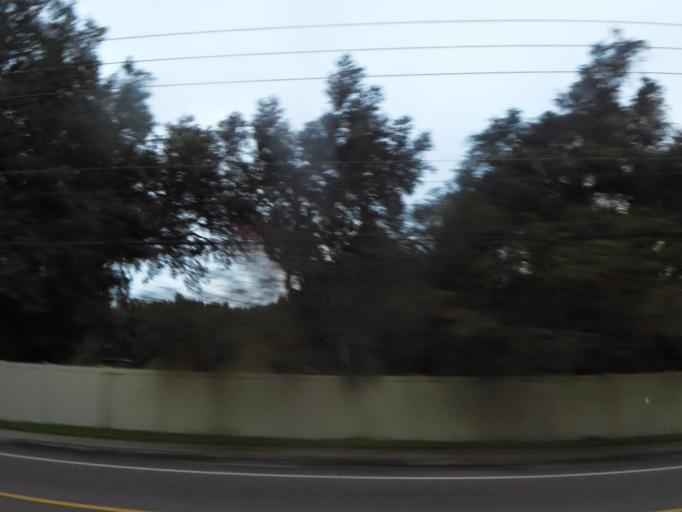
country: US
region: Florida
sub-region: Duval County
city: Jacksonville
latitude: 30.3668
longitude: -81.5649
